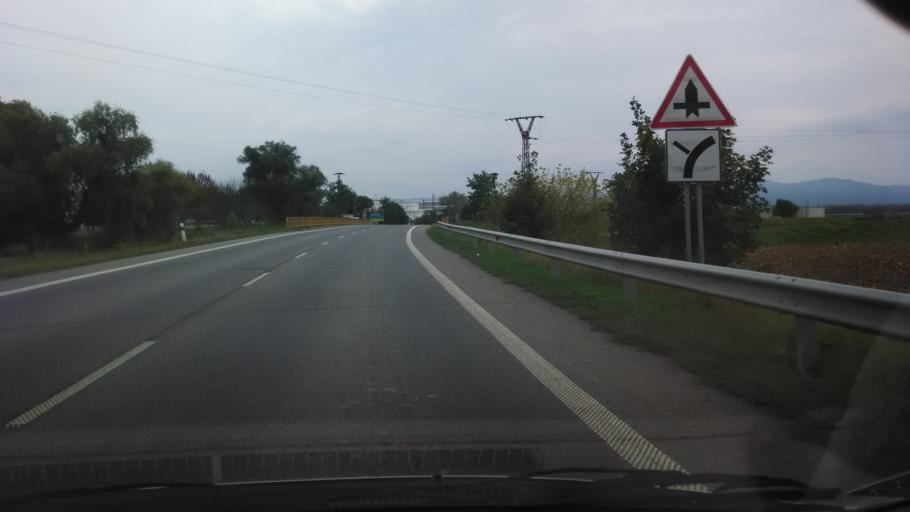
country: SK
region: Banskobystricky
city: Dudince
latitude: 48.1079
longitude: 18.8875
